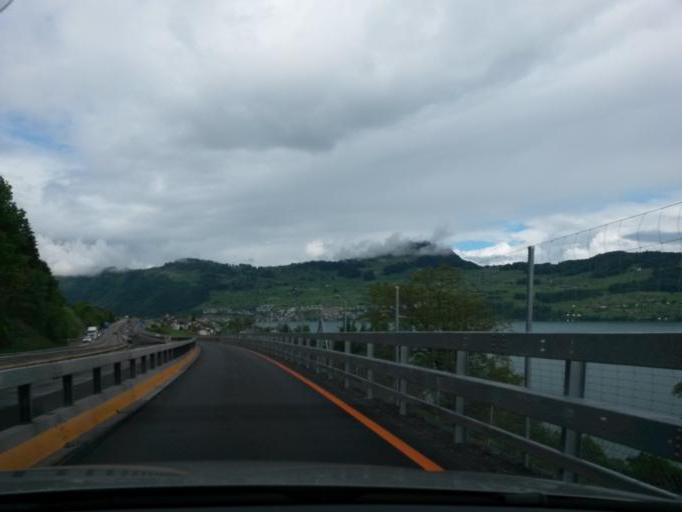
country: CH
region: Nidwalden
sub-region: Nidwalden
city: Beckenried
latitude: 46.9702
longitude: 8.4523
